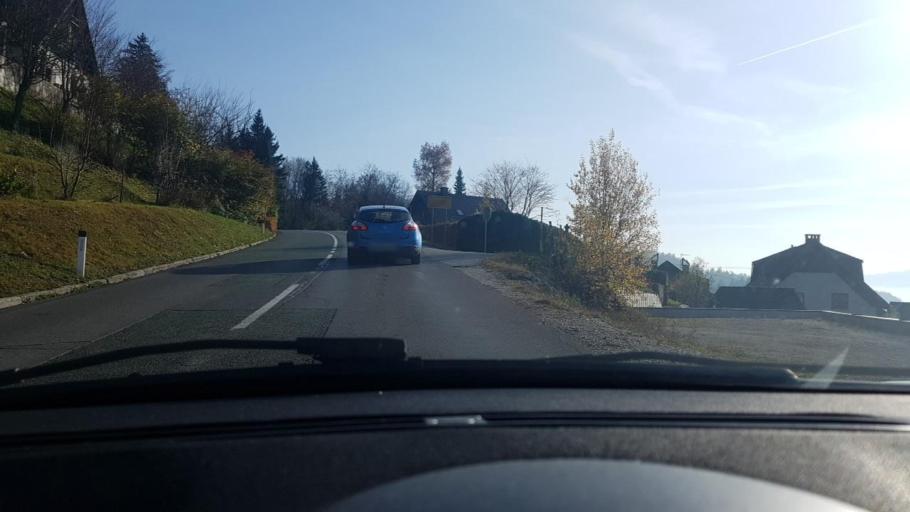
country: SI
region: Trzic
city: Bistrica pri Trzicu
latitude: 46.3361
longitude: 14.3064
